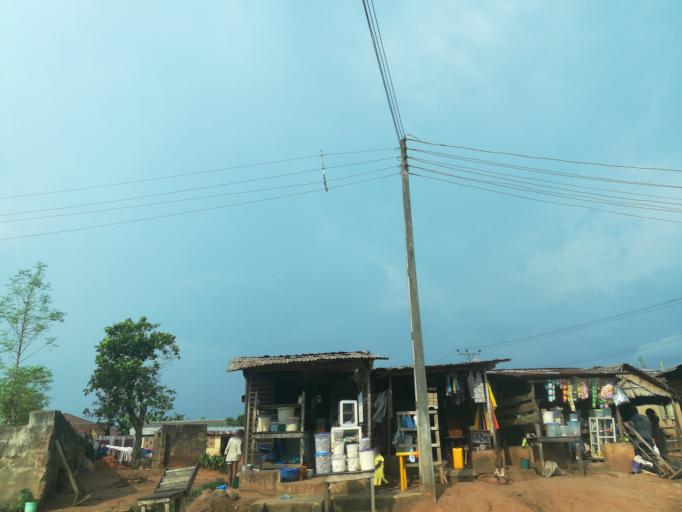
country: NG
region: Lagos
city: Ikorodu
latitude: 6.6645
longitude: 3.6662
